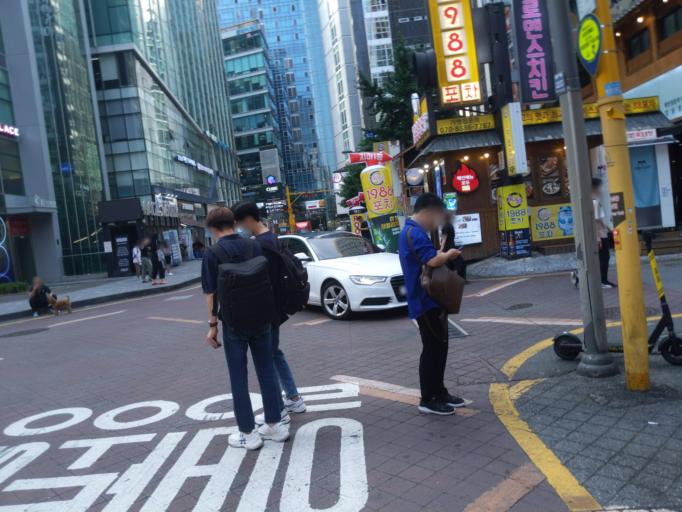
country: KR
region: Seoul
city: Seoul
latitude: 37.5016
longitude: 127.0251
